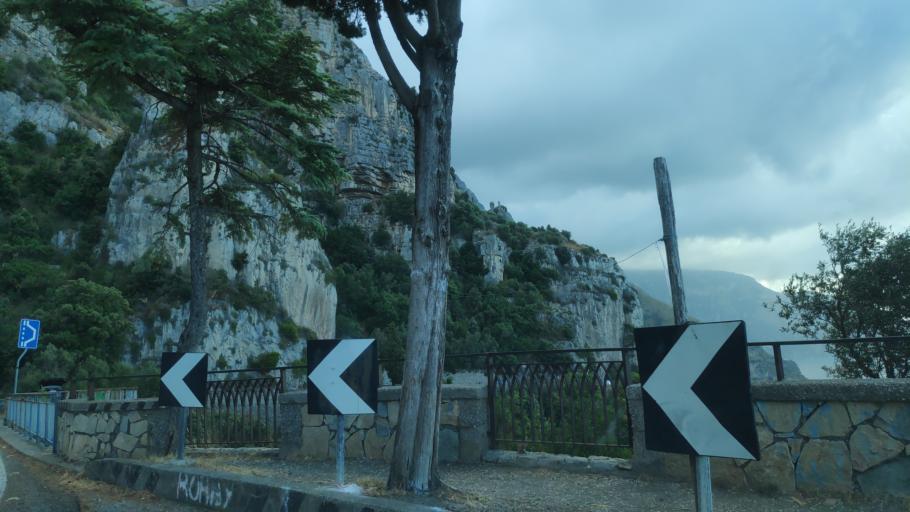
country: IT
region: Campania
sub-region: Provincia di Napoli
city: Arola-Preazzano
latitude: 40.6173
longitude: 14.4403
